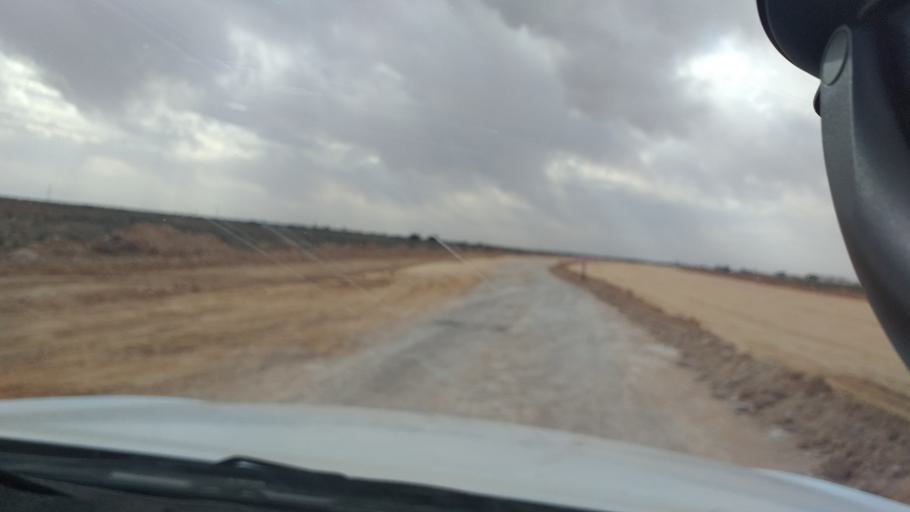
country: TN
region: Madanin
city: Medenine
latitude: 33.3093
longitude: 10.6136
